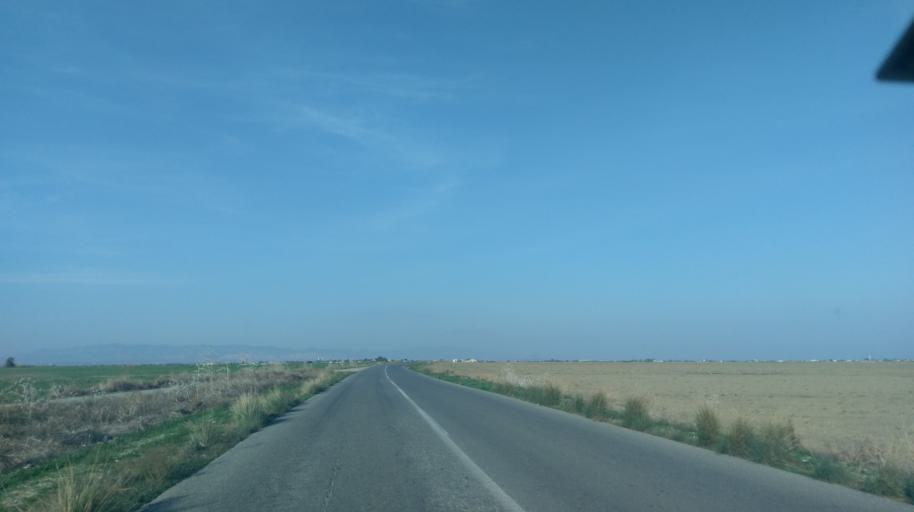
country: CY
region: Ammochostos
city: Achna
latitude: 35.1468
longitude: 33.7478
